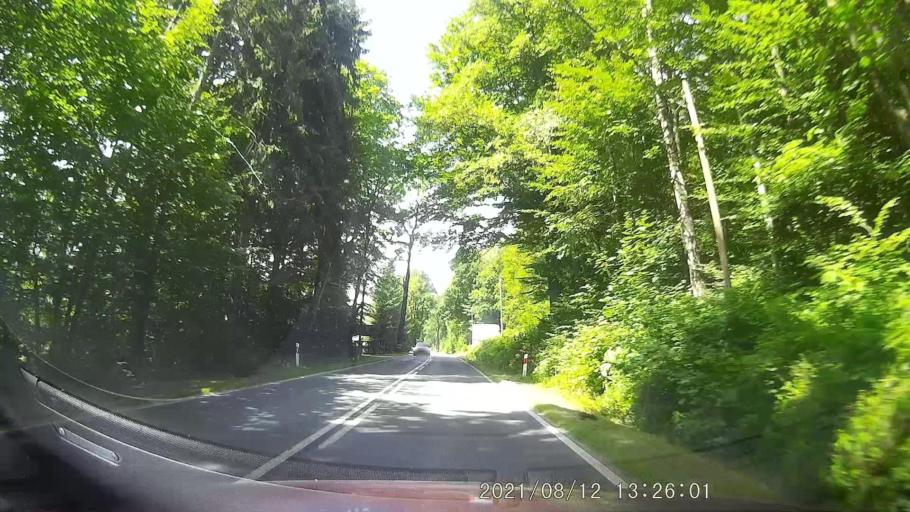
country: PL
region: Lower Silesian Voivodeship
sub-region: Powiat klodzki
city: Ladek-Zdroj
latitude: 50.3255
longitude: 16.8840
